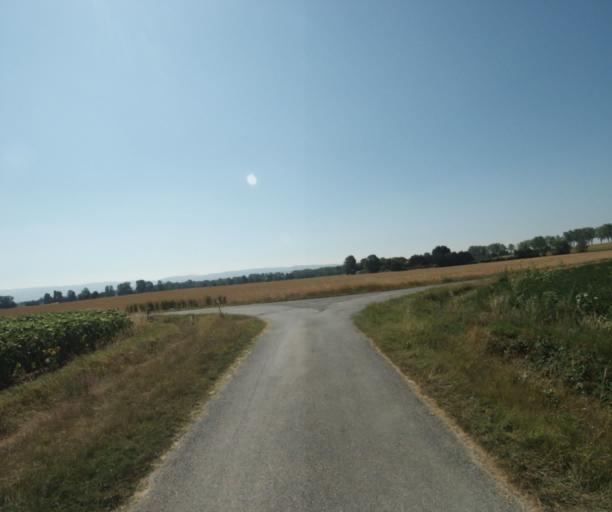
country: FR
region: Midi-Pyrenees
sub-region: Departement de la Haute-Garonne
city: Revel
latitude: 43.5061
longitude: 1.9568
